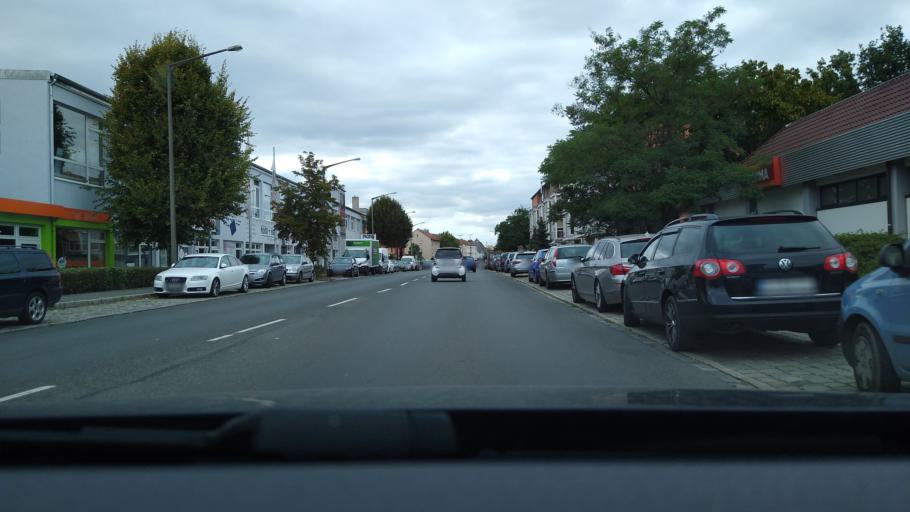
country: DE
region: Bavaria
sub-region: Regierungsbezirk Mittelfranken
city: Wetzendorf
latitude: 49.4713
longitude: 11.0233
